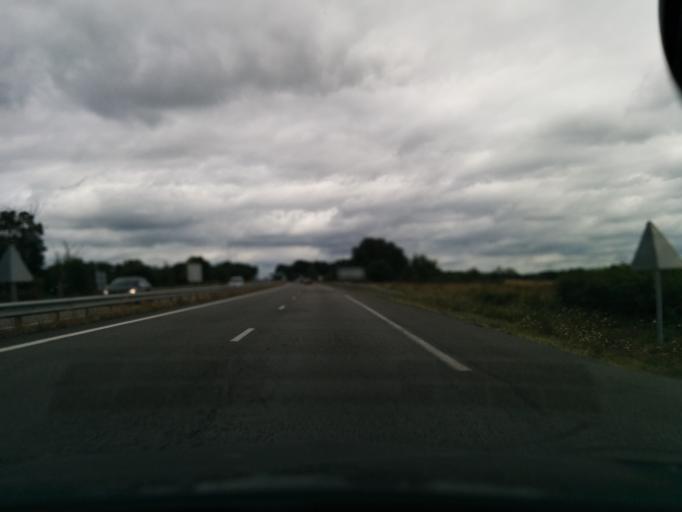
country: FR
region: Limousin
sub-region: Departement de la Creuse
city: Saint-Maurice-la-Souterraine
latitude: 46.1892
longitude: 1.3822
